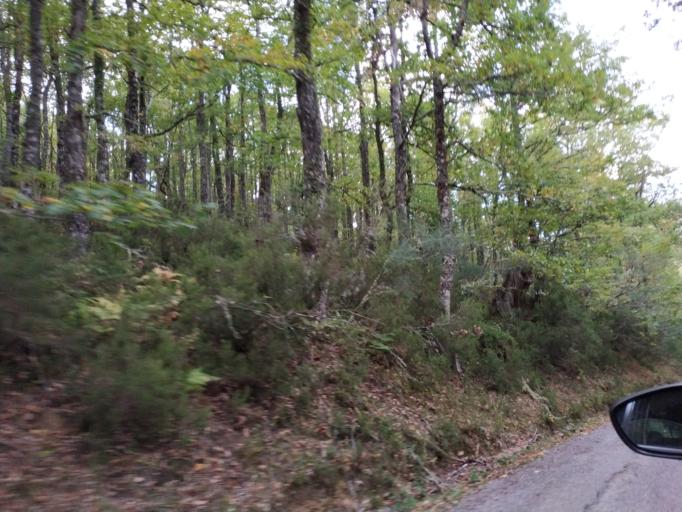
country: ES
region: Castille and Leon
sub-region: Provincia de Leon
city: Candin
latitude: 42.8639
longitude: -6.8615
